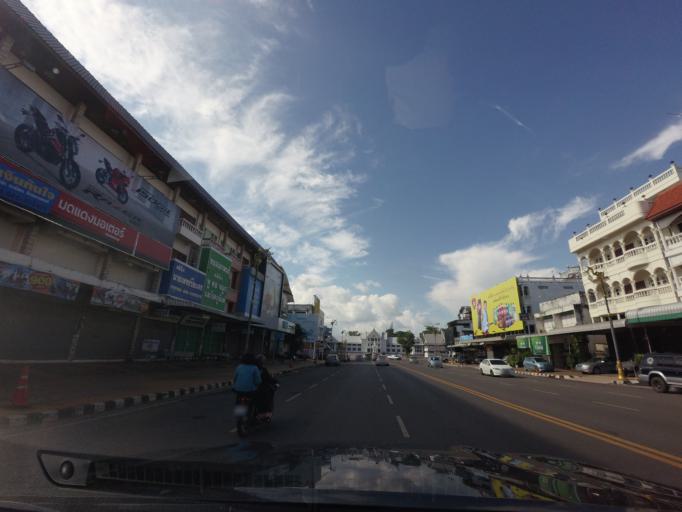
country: TH
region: Nong Khai
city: Nong Khai
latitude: 17.8780
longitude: 102.7413
